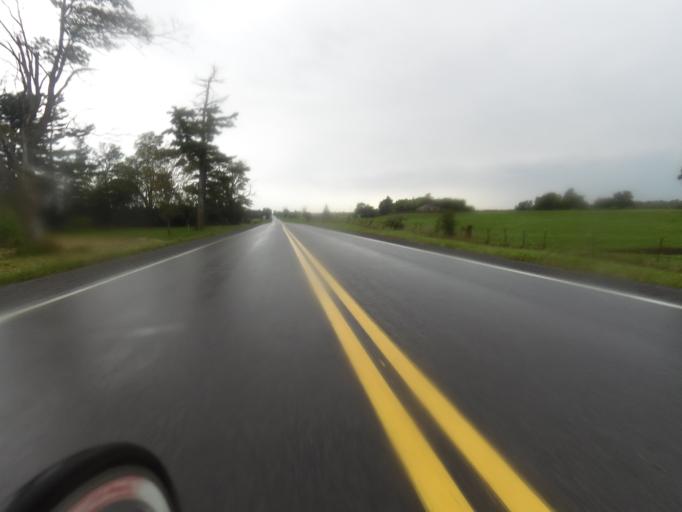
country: CA
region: Ontario
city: Bells Corners
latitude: 45.1777
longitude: -75.6642
